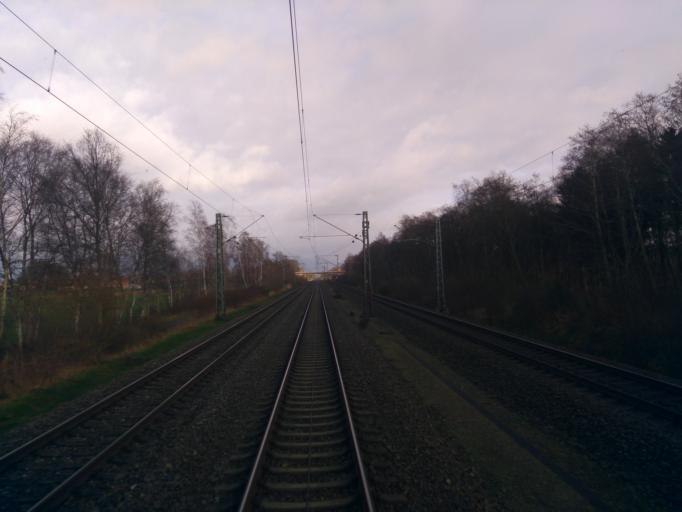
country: DE
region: Lower Saxony
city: Konigsmoor
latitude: 53.2281
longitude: 9.6369
